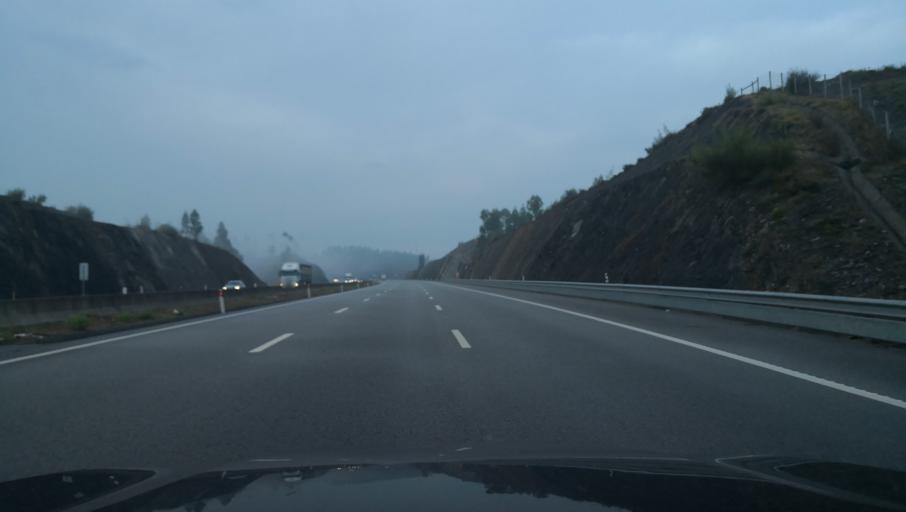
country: PT
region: Porto
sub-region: Paredes
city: Recarei
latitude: 41.1321
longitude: -8.4279
